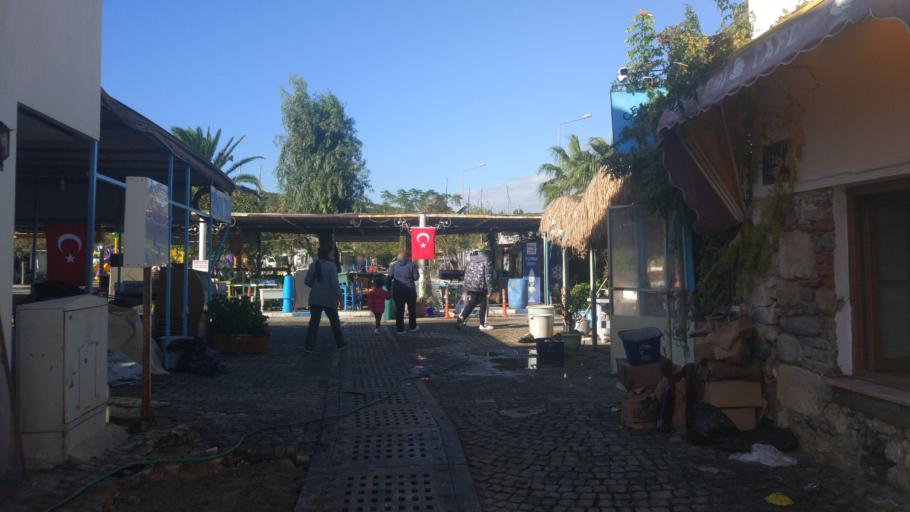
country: TR
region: Izmir
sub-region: Seferihisar
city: Seferhisar
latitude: 38.1938
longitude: 26.7846
